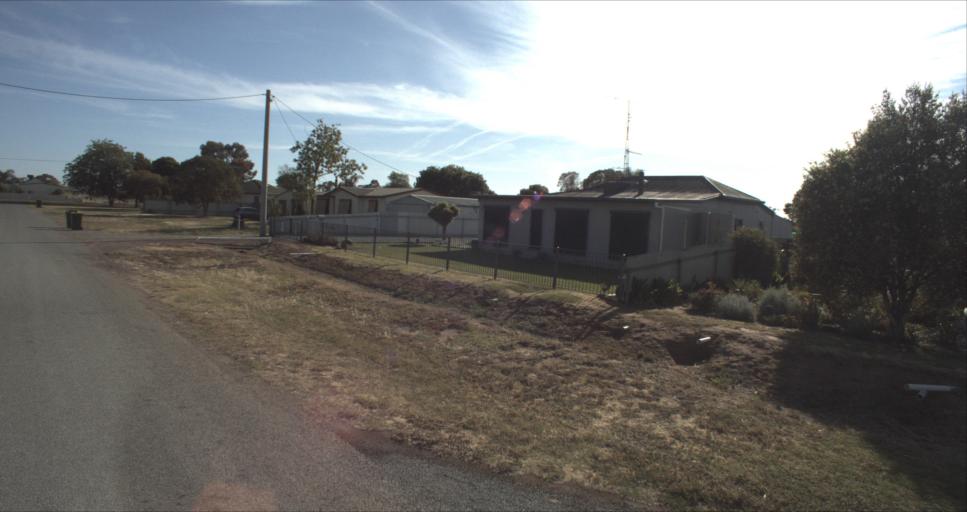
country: AU
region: New South Wales
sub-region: Leeton
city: Leeton
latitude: -34.5952
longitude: 146.4083
